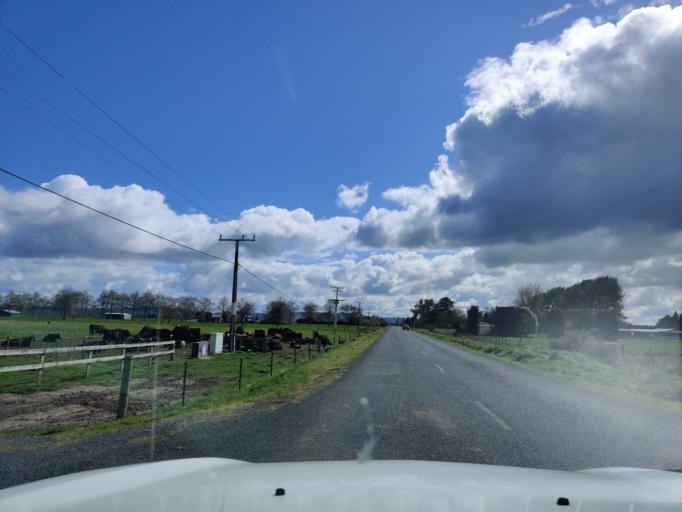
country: NZ
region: Waikato
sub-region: Waikato District
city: Ngaruawahia
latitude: -37.6071
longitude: 175.3063
